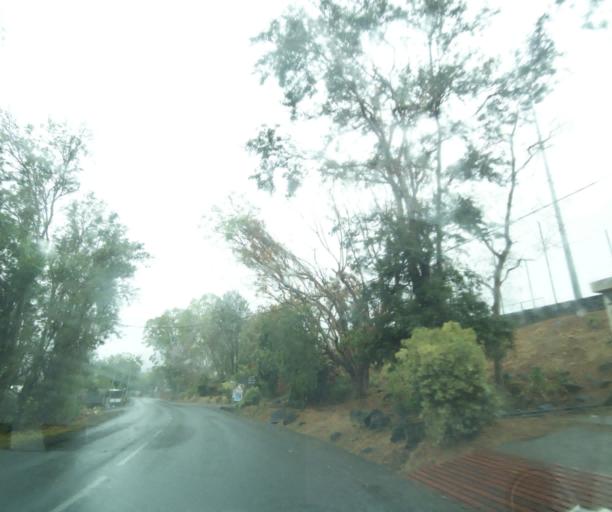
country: RE
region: Reunion
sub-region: Reunion
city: Saint-Paul
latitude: -21.0182
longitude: 55.3025
